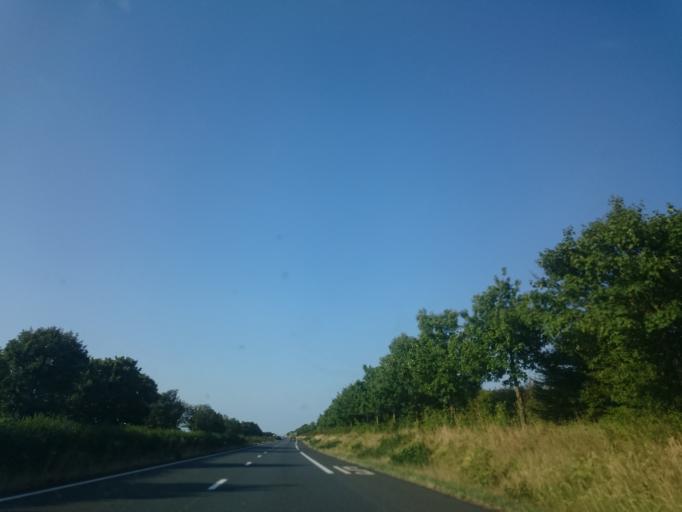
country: FR
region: Centre
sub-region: Departement de l'Indre
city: Vatan
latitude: 47.0113
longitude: 1.7820
